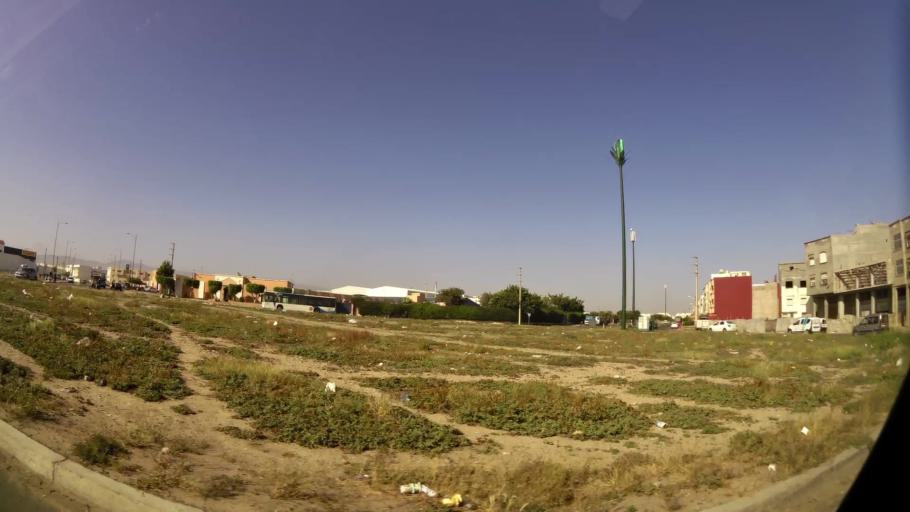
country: MA
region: Souss-Massa-Draa
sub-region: Inezgane-Ait Mellou
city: Inezgane
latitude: 30.3803
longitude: -9.5181
